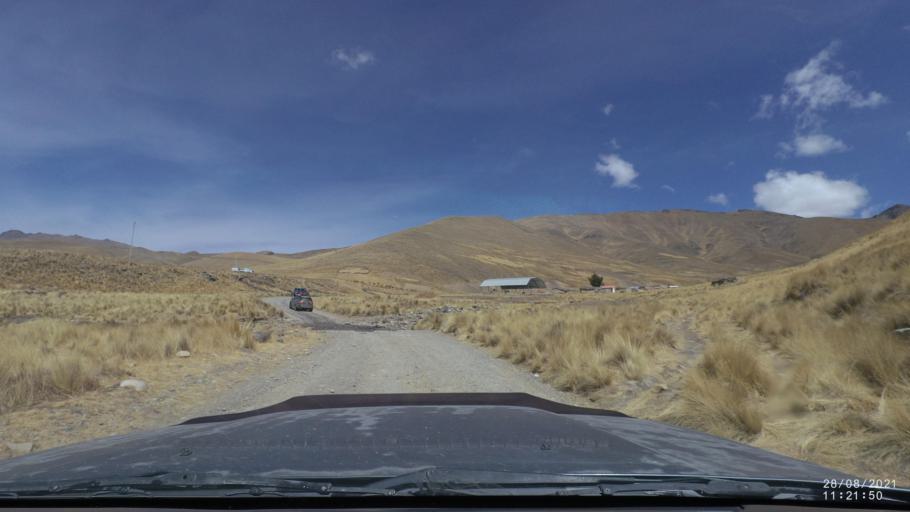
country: BO
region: Cochabamba
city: Sipe Sipe
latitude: -17.1647
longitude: -66.3495
